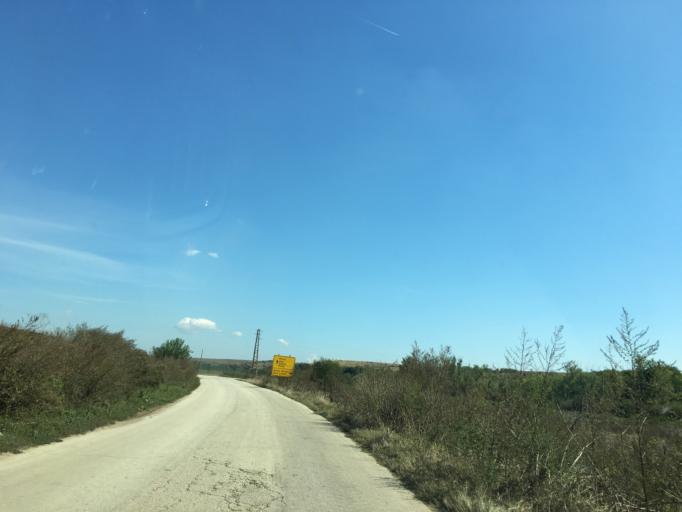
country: BG
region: Pleven
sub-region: Obshtina Knezha
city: Knezha
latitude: 43.5514
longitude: 24.1780
